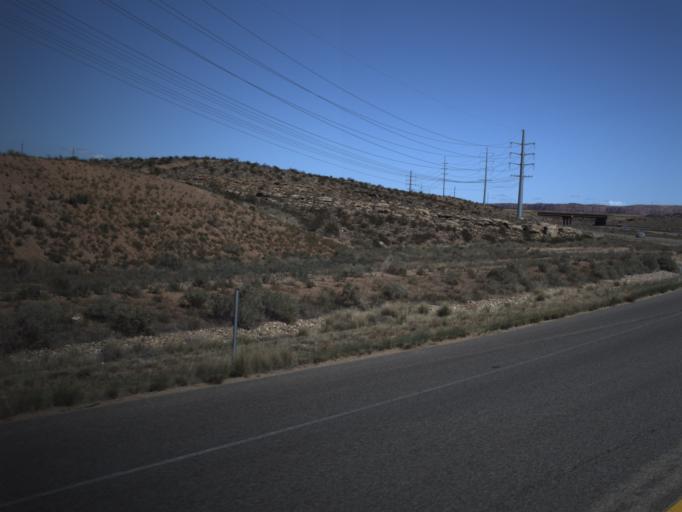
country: US
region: Utah
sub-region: Washington County
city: Washington
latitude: 37.0106
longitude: -113.5000
